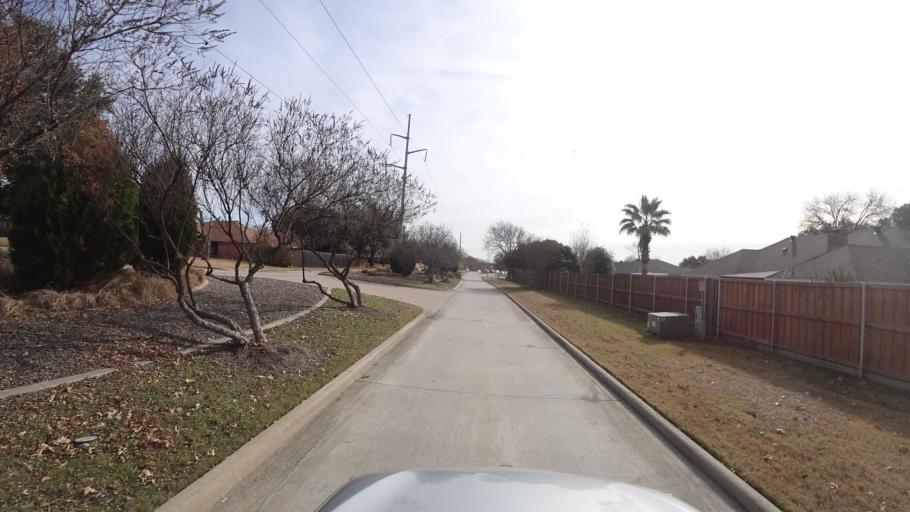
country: US
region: Texas
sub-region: Denton County
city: Highland Village
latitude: 33.0836
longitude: -97.0460
